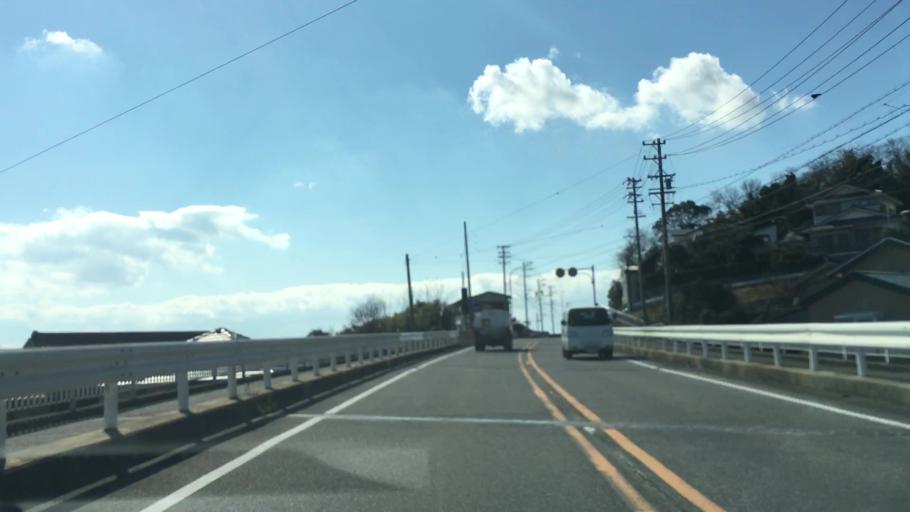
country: JP
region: Aichi
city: Nishio
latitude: 34.7956
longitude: 137.1232
